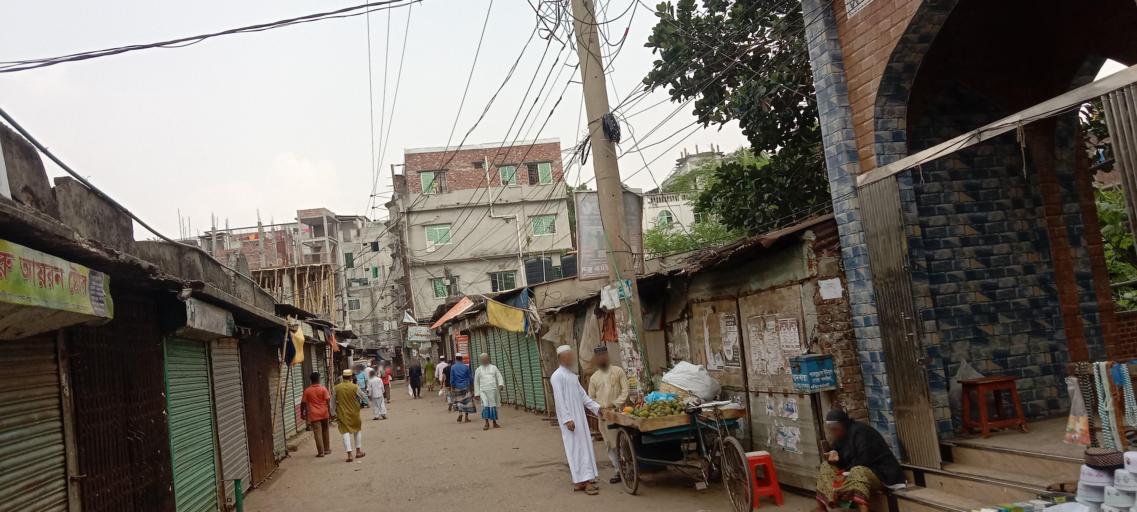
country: BD
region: Dhaka
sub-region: Dhaka
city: Dhaka
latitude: 23.7088
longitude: 90.3965
